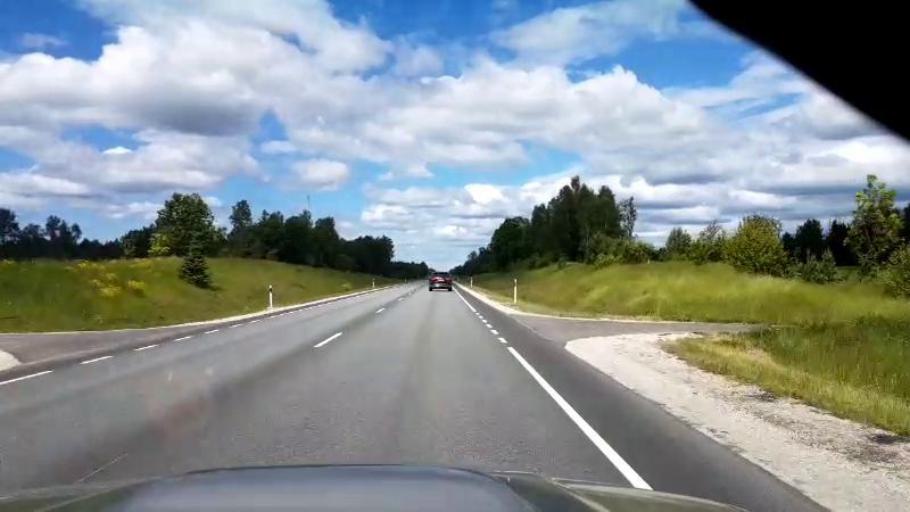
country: EE
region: Harju
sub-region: Nissi vald
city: Riisipere
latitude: 59.0536
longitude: 24.4460
